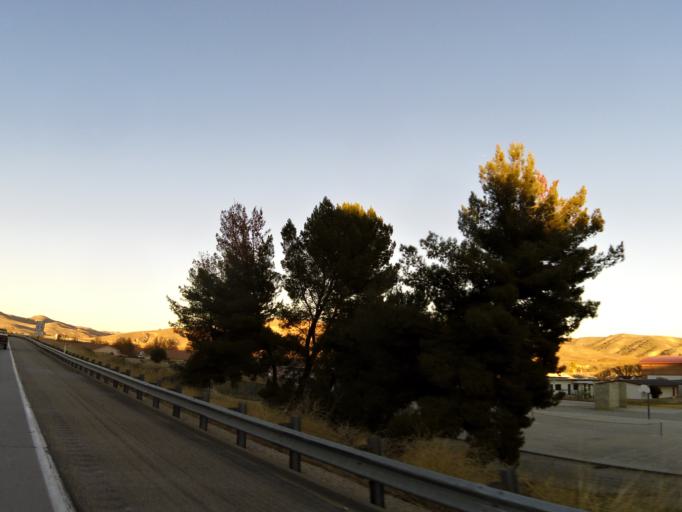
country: US
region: California
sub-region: San Luis Obispo County
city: San Miguel
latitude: 35.7572
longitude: -120.6989
